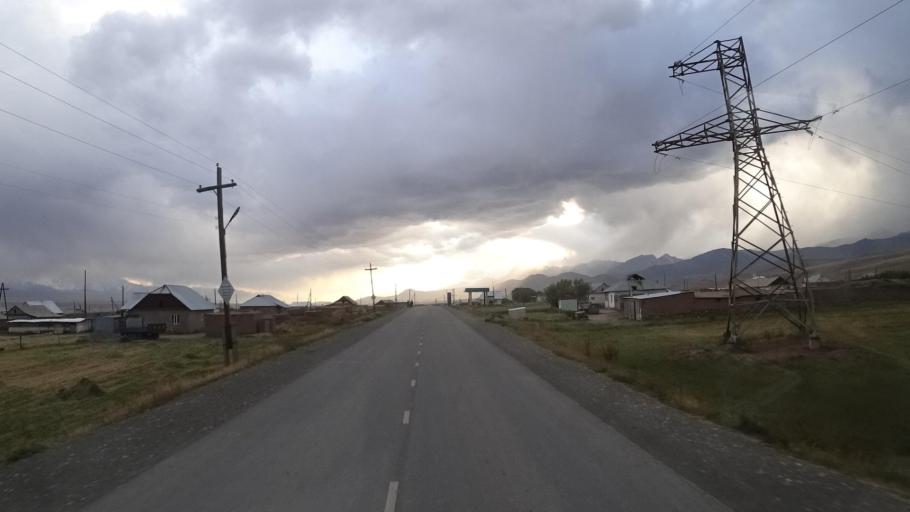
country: KG
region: Osh
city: Osh
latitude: 39.6777
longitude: 72.8851
